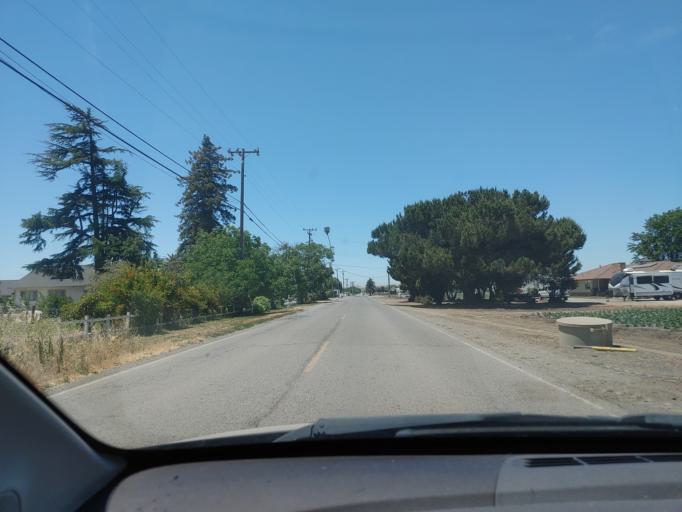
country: US
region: California
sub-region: San Benito County
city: Hollister
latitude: 36.8691
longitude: -121.3948
